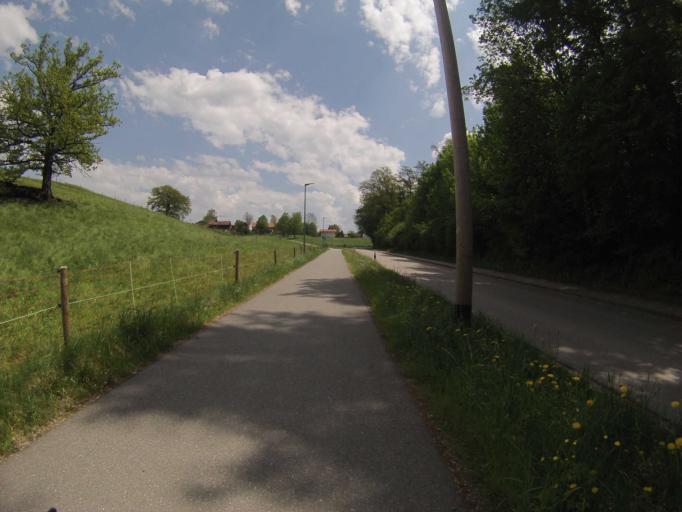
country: DE
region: Bavaria
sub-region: Upper Bavaria
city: Aying
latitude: 47.9450
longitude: 11.7859
